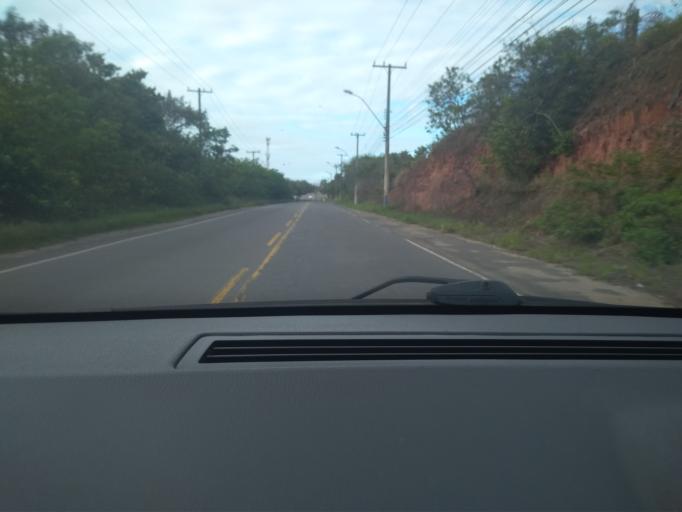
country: BR
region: Espirito Santo
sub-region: Serra
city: Serra
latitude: -20.0995
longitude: -40.1760
